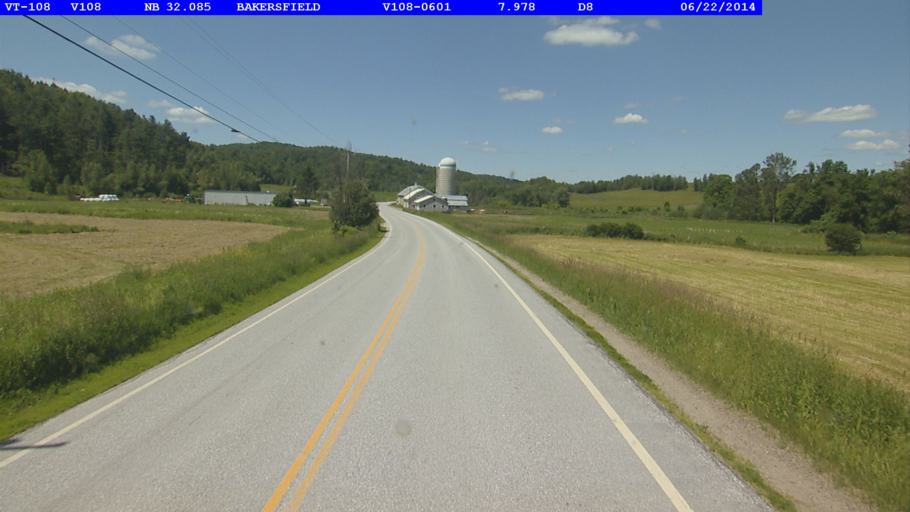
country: US
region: Vermont
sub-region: Franklin County
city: Enosburg Falls
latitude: 44.8377
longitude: -72.8048
